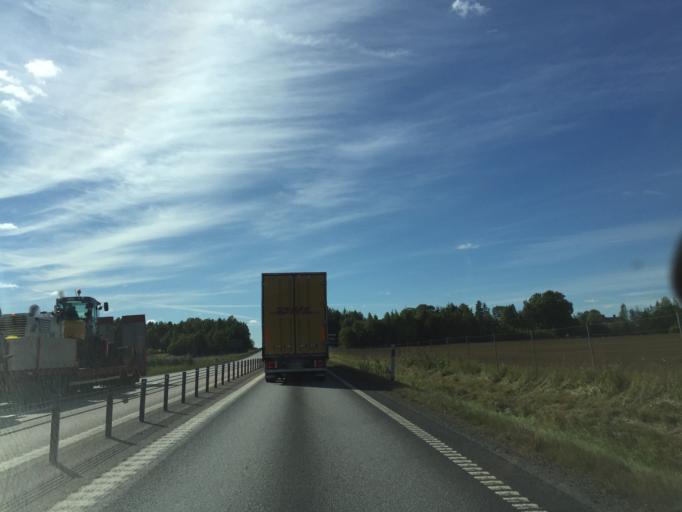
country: SE
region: Vaestmanland
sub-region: Kopings Kommun
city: Koping
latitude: 59.5349
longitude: 15.9907
